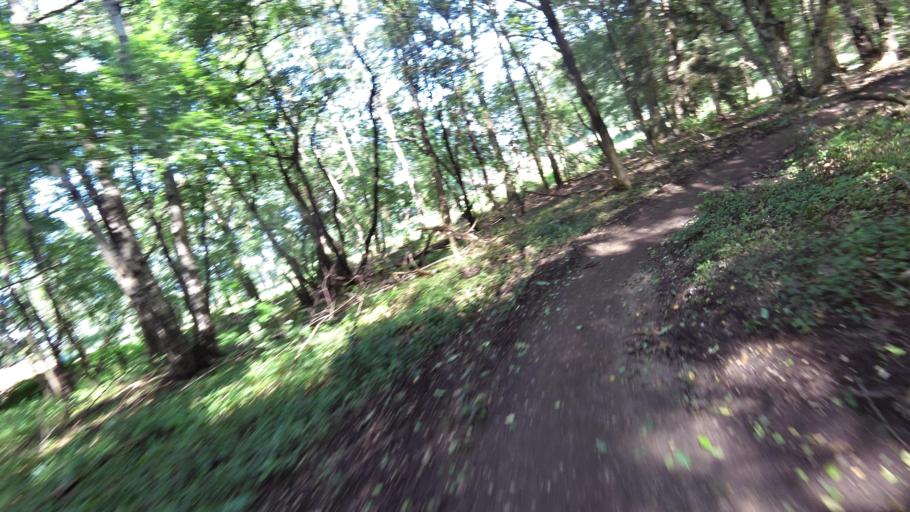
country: NL
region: Gelderland
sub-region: Gemeente Renkum
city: Oosterbeek
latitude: 51.9994
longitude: 5.8281
